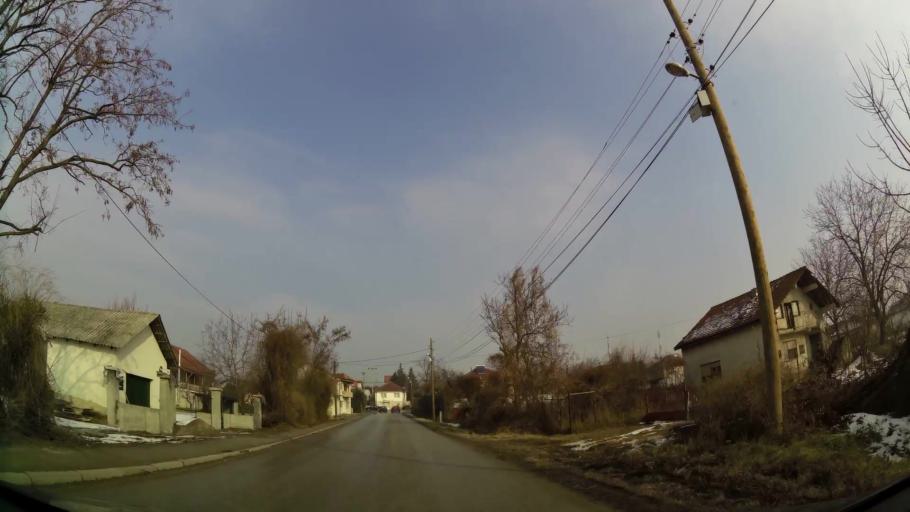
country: MK
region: Ilinden
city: Marino
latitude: 41.9902
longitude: 21.5893
